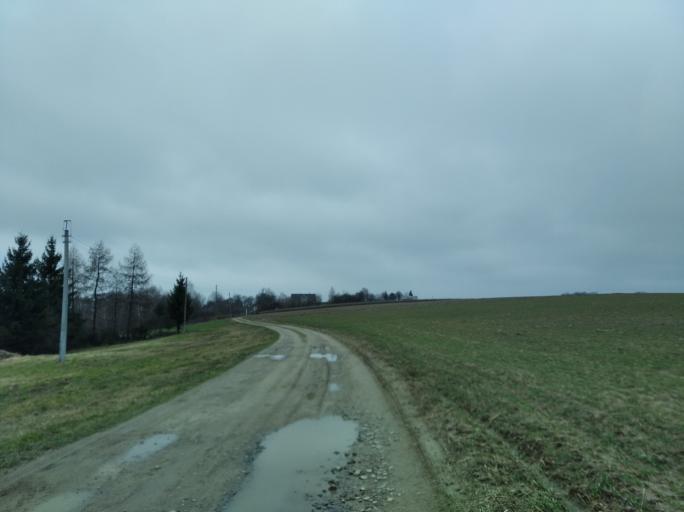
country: PL
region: Subcarpathian Voivodeship
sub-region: Powiat strzyzowski
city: Strzyzow
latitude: 49.8853
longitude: 21.7985
